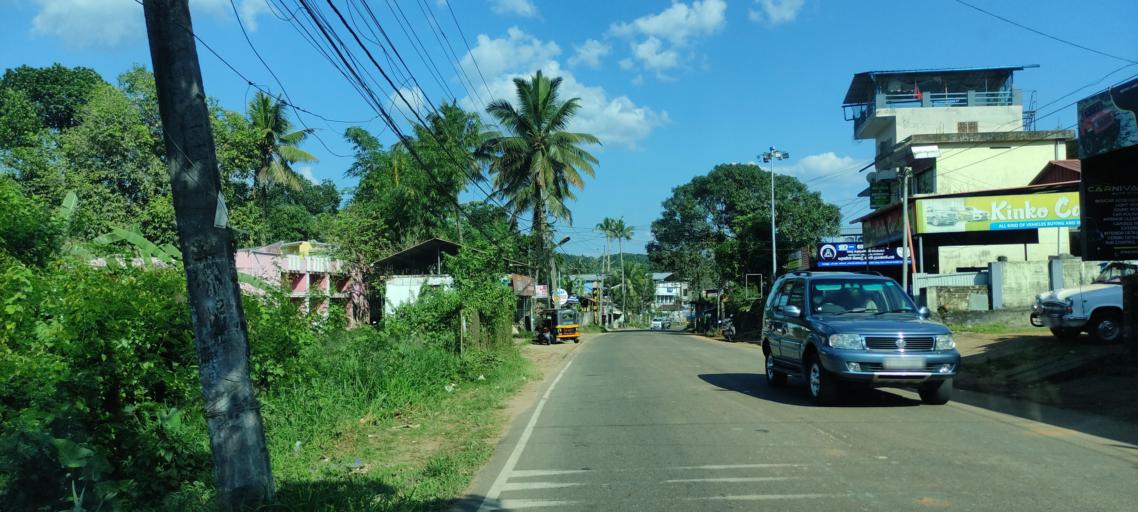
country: IN
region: Kerala
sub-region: Pattanamtitta
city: Pathanamthitta
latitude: 9.2682
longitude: 76.7962
